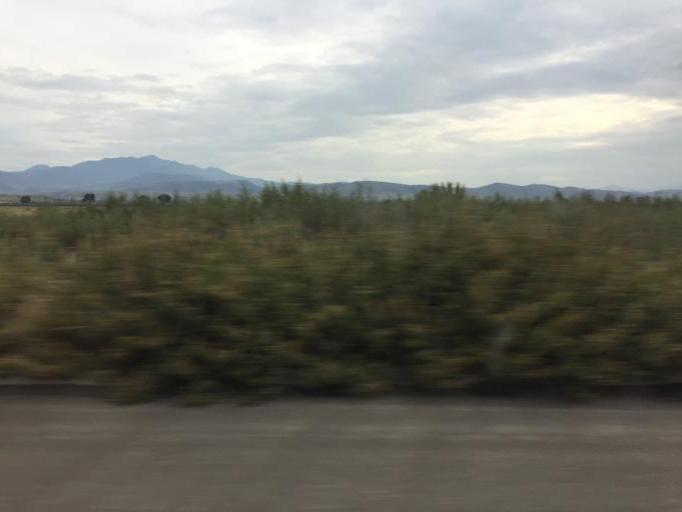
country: MX
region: Mexico
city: Huaniqueo de Morales
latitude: 19.8906
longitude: -101.5293
